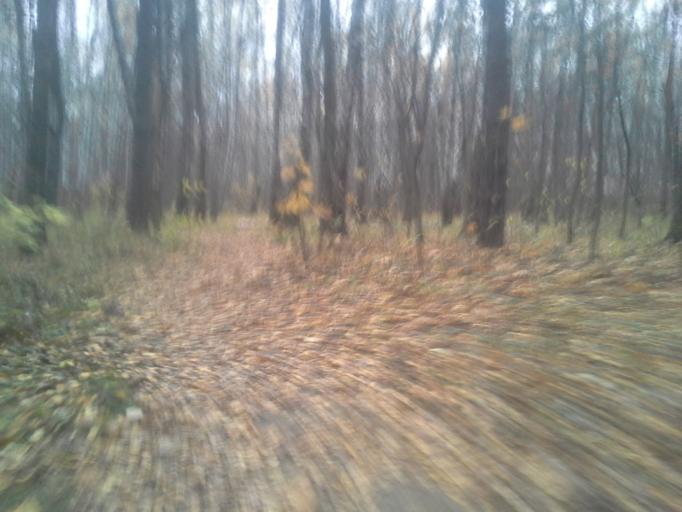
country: RU
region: Moskovskaya
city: Zarech'ye
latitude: 55.6645
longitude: 37.4054
